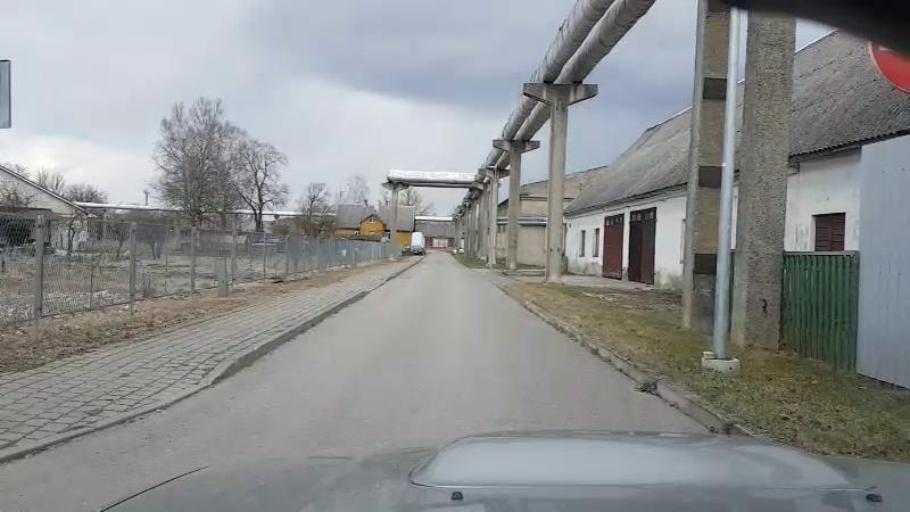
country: EE
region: Jaervamaa
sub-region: Paide linn
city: Paide
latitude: 58.8830
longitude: 25.5575
